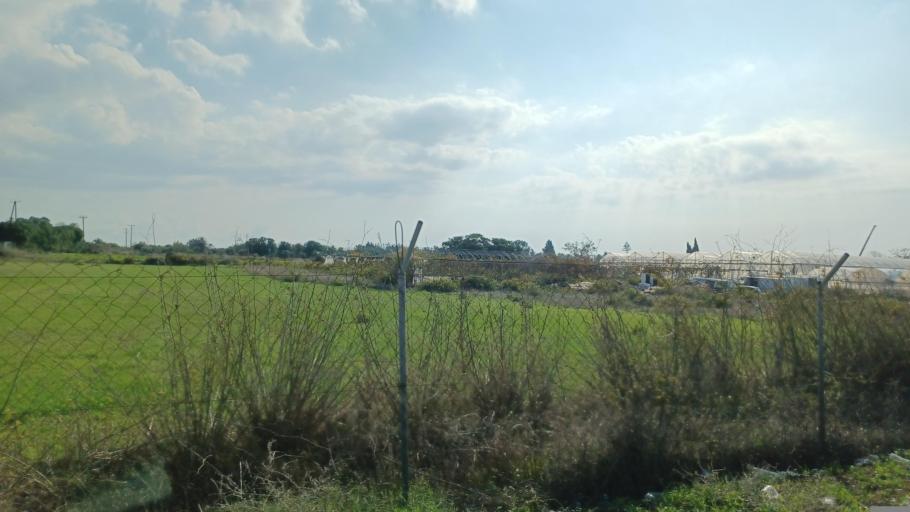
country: CY
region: Pafos
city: Empa
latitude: 34.8130
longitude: 32.4122
